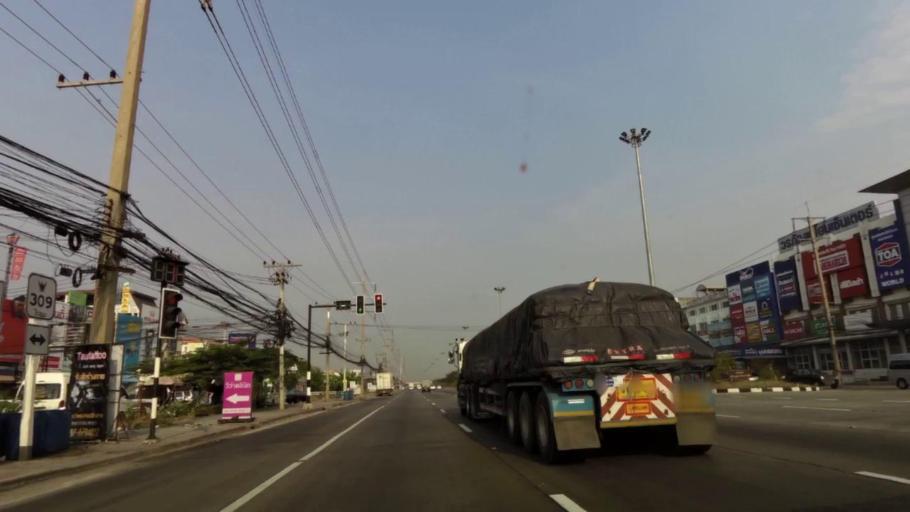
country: TH
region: Phra Nakhon Si Ayutthaya
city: Uthai
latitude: 14.3238
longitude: 100.6296
